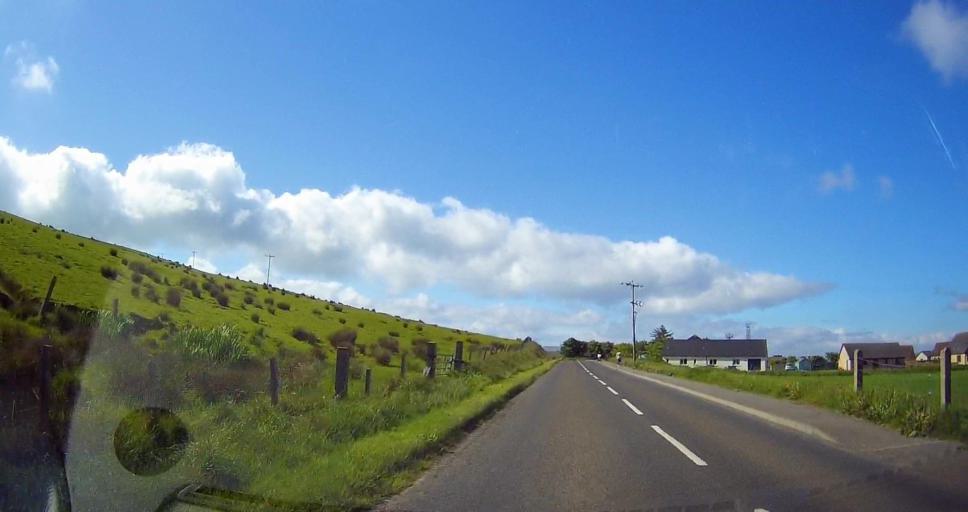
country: GB
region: Scotland
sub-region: Orkney Islands
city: Orkney
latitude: 58.9632
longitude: -2.9674
